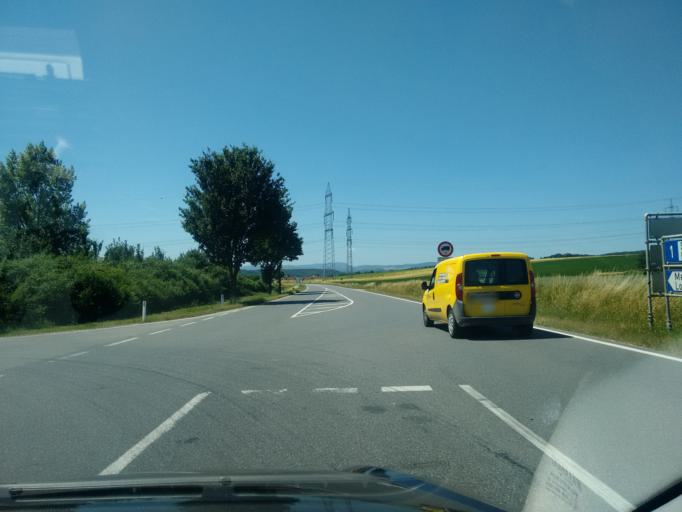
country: AT
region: Lower Austria
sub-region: Politischer Bezirk Melk
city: Loosdorf
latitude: 48.1965
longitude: 15.4213
